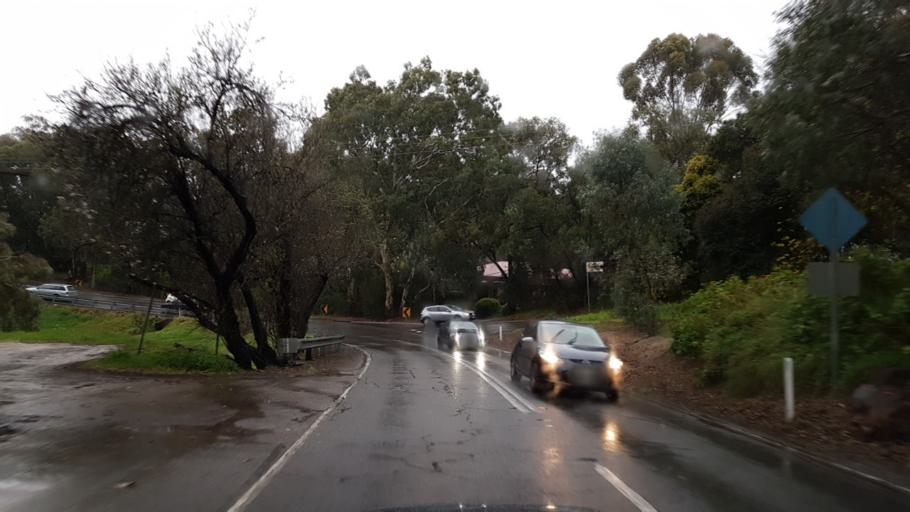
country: AU
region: South Australia
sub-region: Onkaparinga
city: Craigburn Farm
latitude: -35.0490
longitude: 138.6199
